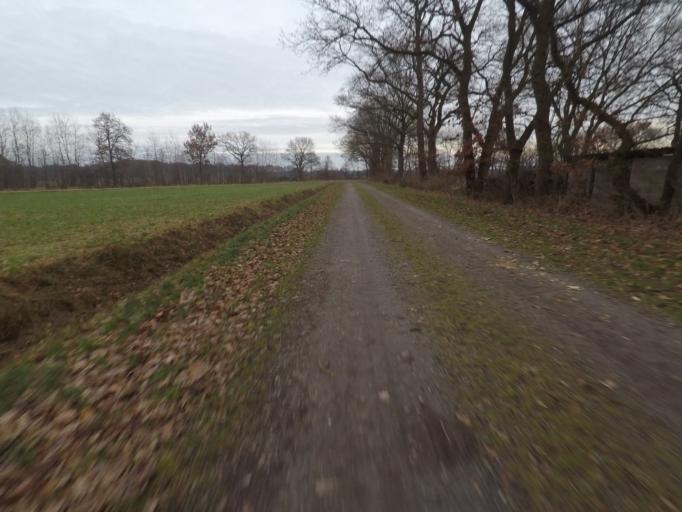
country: DE
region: Lower Saxony
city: Langen
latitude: 53.6076
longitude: 8.6232
